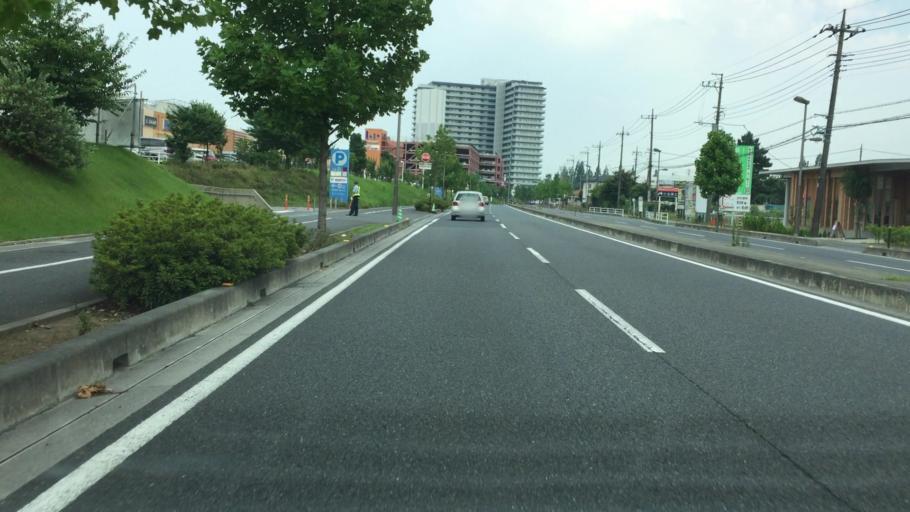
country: JP
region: Saitama
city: Yoshikawa
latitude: 35.8601
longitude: 139.8636
